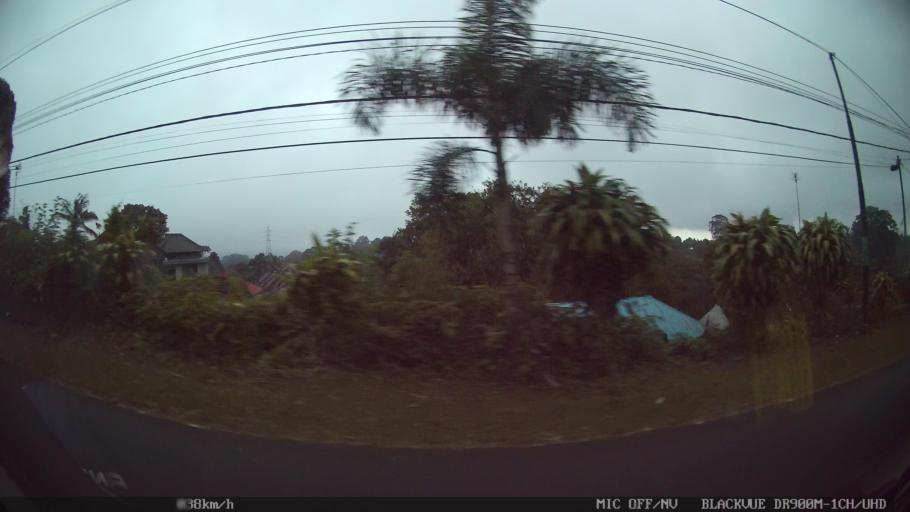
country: ID
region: Bali
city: Klau
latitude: -8.3467
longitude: 115.0293
